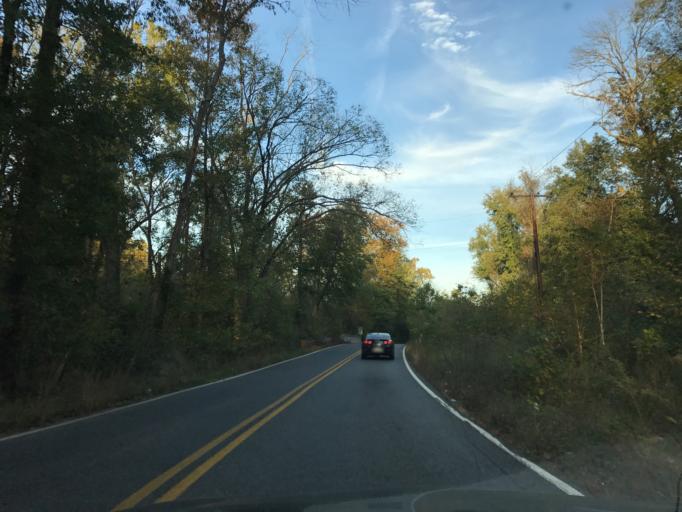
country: US
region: Maryland
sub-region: Prince George's County
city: South Laurel
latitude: 39.0713
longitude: -76.8388
